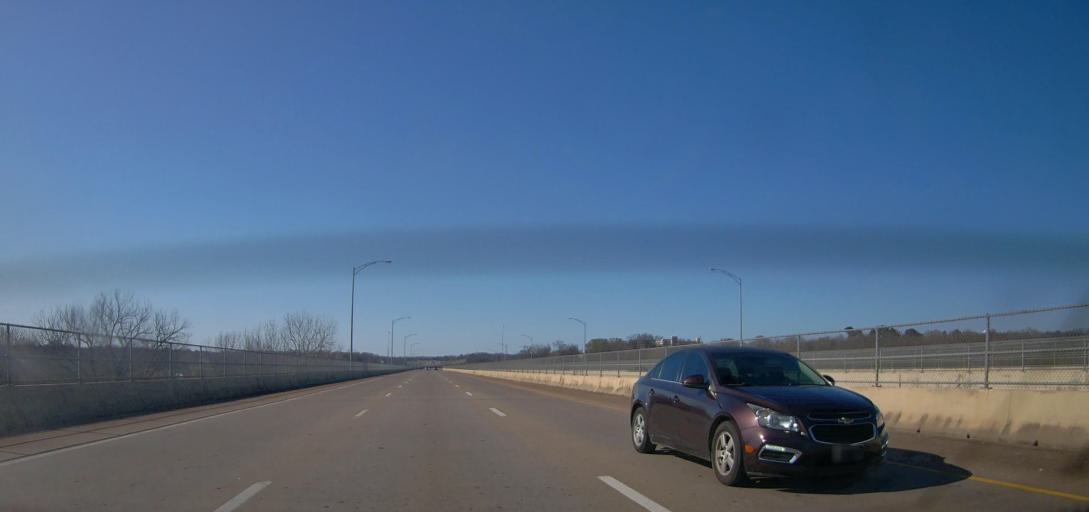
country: US
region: Alabama
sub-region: Lauderdale County
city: East Florence
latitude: 34.7978
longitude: -87.6481
